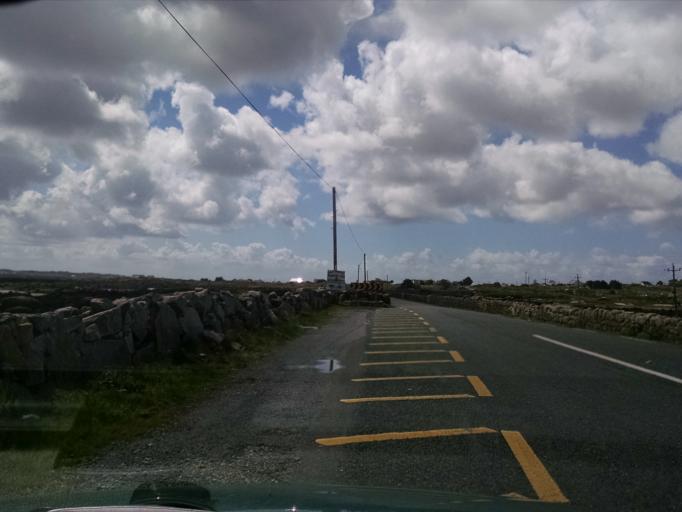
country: IE
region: Connaught
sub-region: County Galway
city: Oughterard
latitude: 53.3061
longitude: -9.6344
